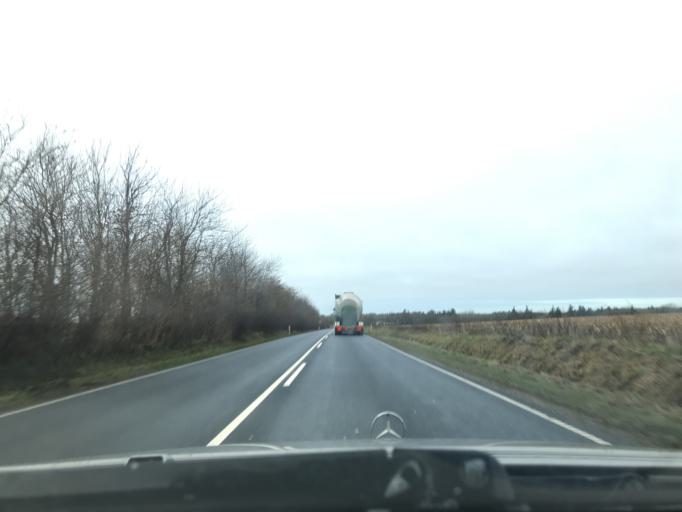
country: DK
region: South Denmark
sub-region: Esbjerg Kommune
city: Ribe
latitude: 55.2870
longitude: 8.8313
